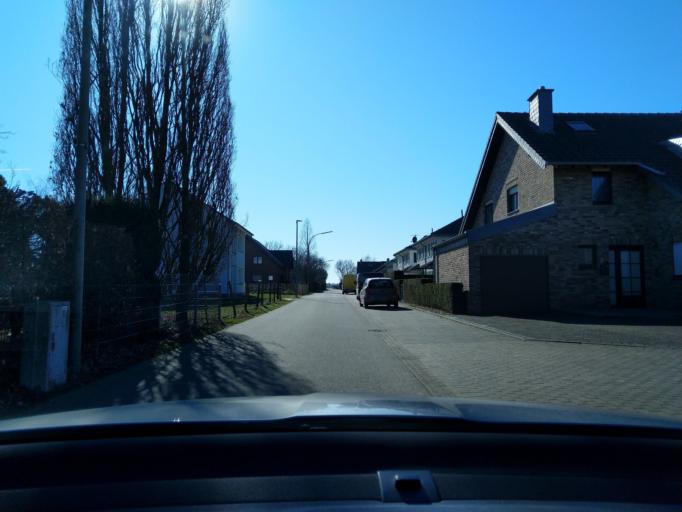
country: DE
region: North Rhine-Westphalia
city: Wegberg
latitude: 51.1298
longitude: 6.3285
